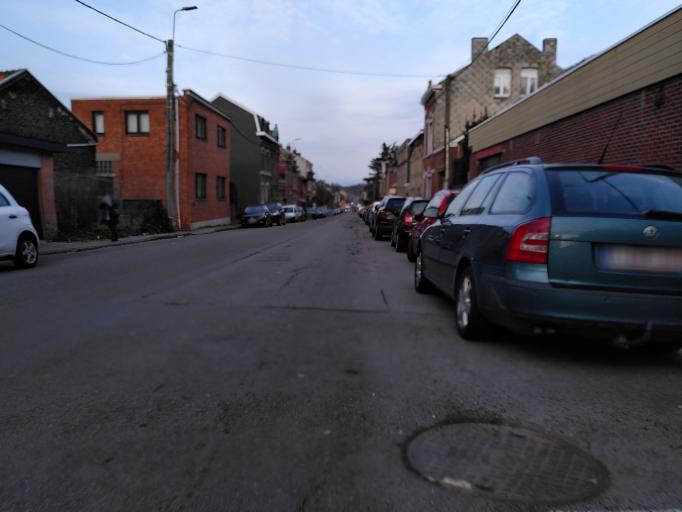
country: BE
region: Wallonia
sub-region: Province de Liege
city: Herstal
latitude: 50.6596
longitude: 5.6529
